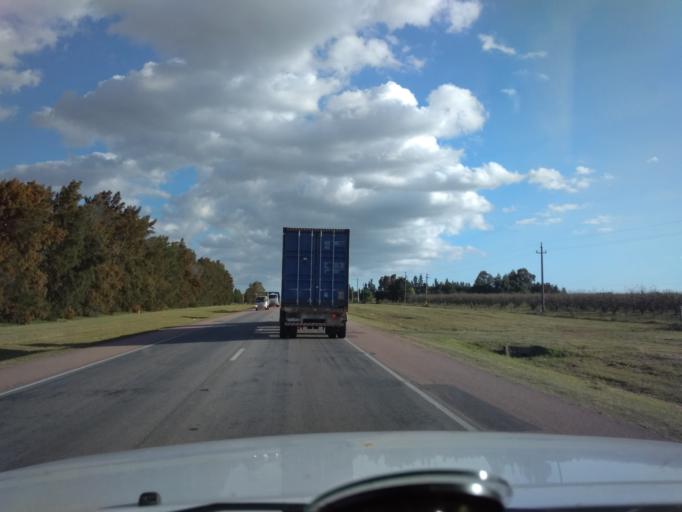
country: UY
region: Canelones
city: Canelones
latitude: -34.4005
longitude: -56.2572
